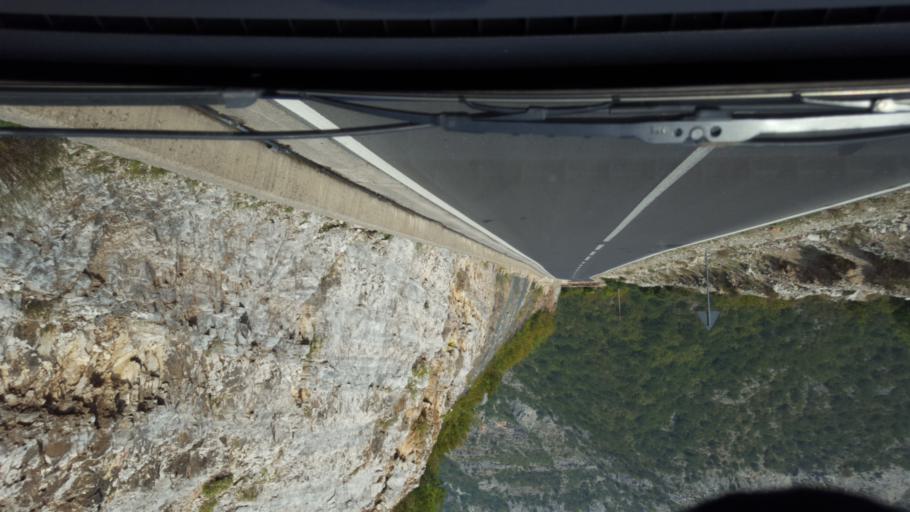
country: AL
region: Shkoder
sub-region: Rrethi i Malesia e Madhe
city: Kastrat
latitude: 42.4206
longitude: 19.5108
